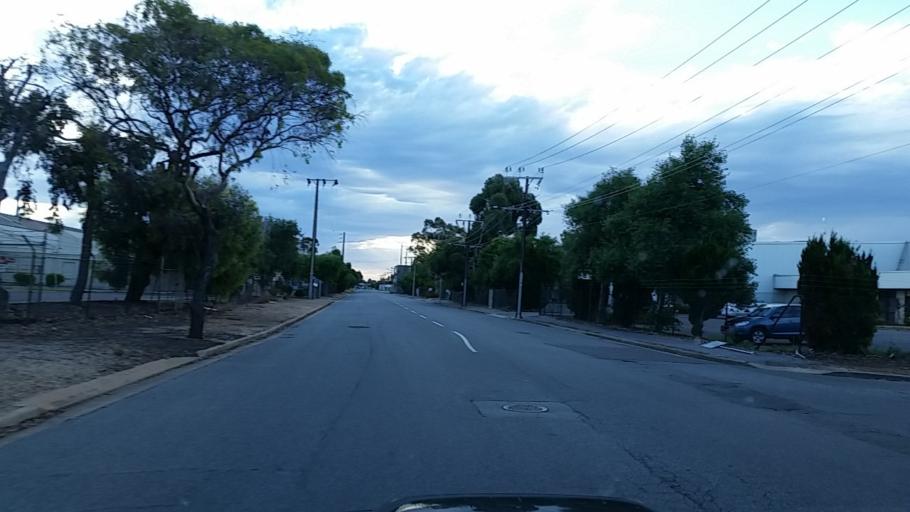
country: AU
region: South Australia
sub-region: Charles Sturt
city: Woodville North
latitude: -34.8628
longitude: 138.5410
